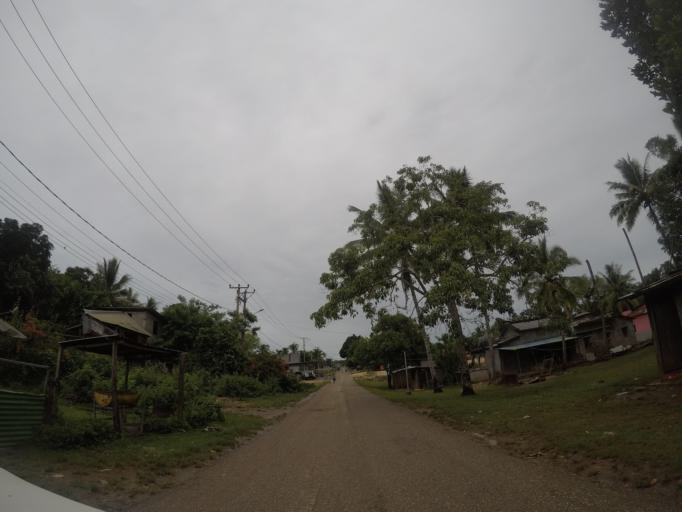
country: TL
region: Lautem
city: Lospalos
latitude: -8.5198
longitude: 127.0032
